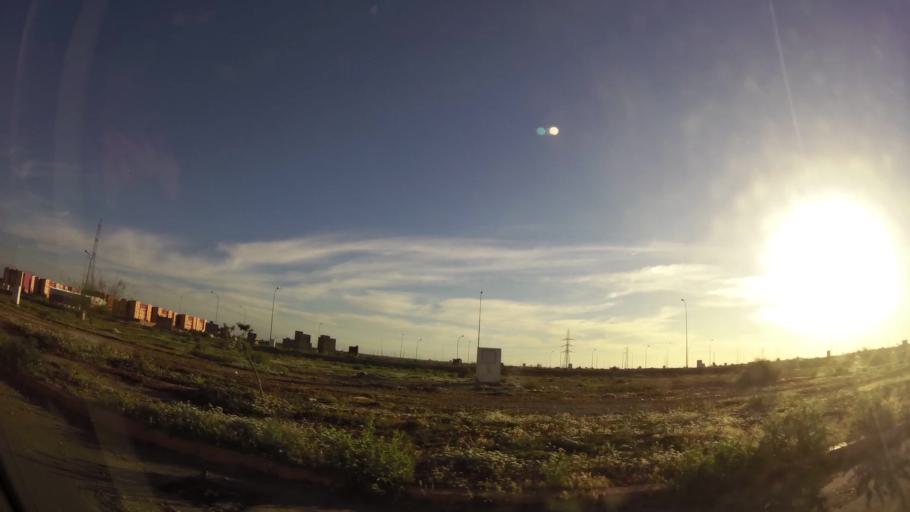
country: MA
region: Marrakech-Tensift-Al Haouz
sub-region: Marrakech
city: Marrakesh
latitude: 31.7451
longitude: -8.1269
